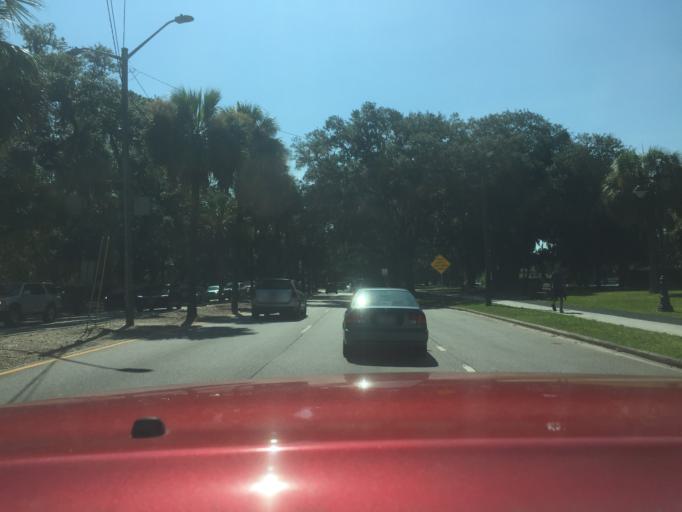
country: US
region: Georgia
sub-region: Chatham County
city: Thunderbolt
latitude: 32.0481
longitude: -81.0851
